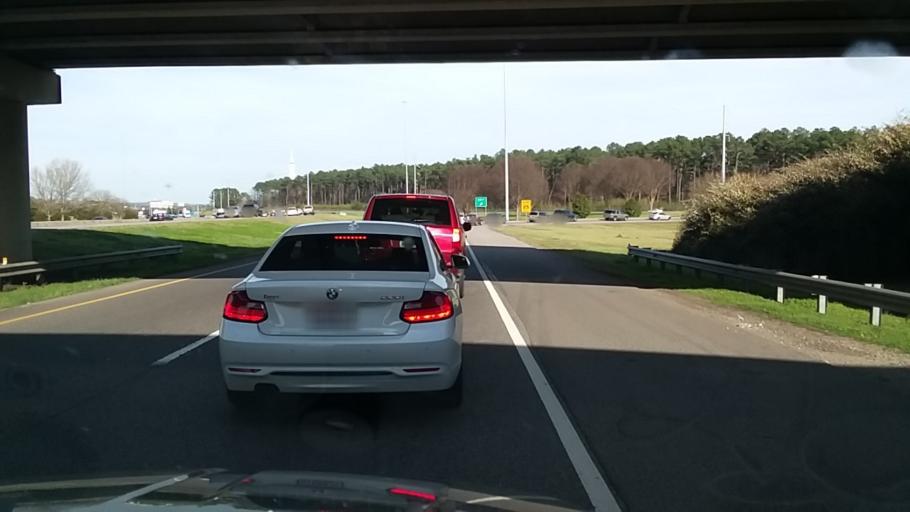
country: US
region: Alabama
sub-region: Madison County
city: Redstone Arsenal
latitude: 34.7065
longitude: -86.6713
